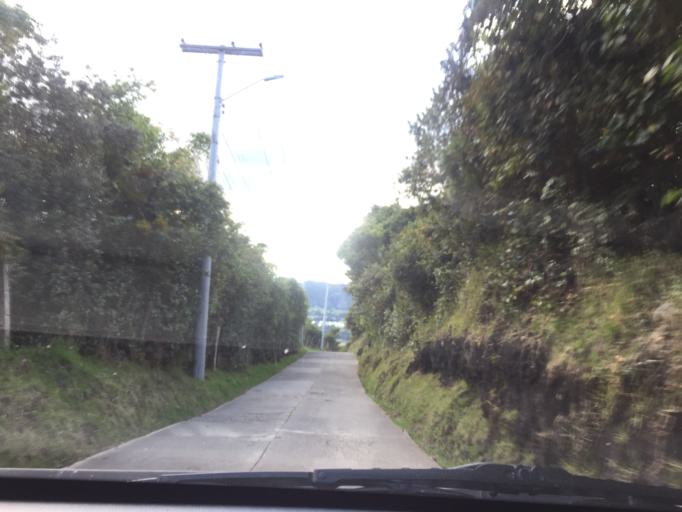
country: CO
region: Cundinamarca
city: Sopo
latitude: 4.9146
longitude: -73.9296
